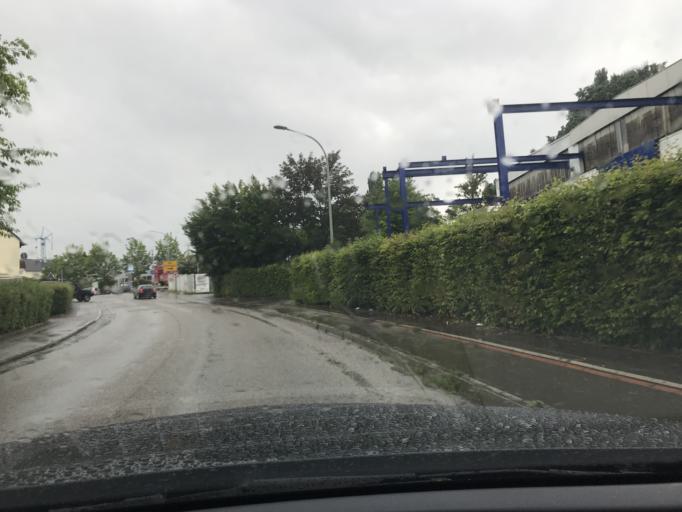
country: DE
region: Baden-Wuerttemberg
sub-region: Regierungsbezirk Stuttgart
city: Winnenden
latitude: 48.8770
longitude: 9.3907
